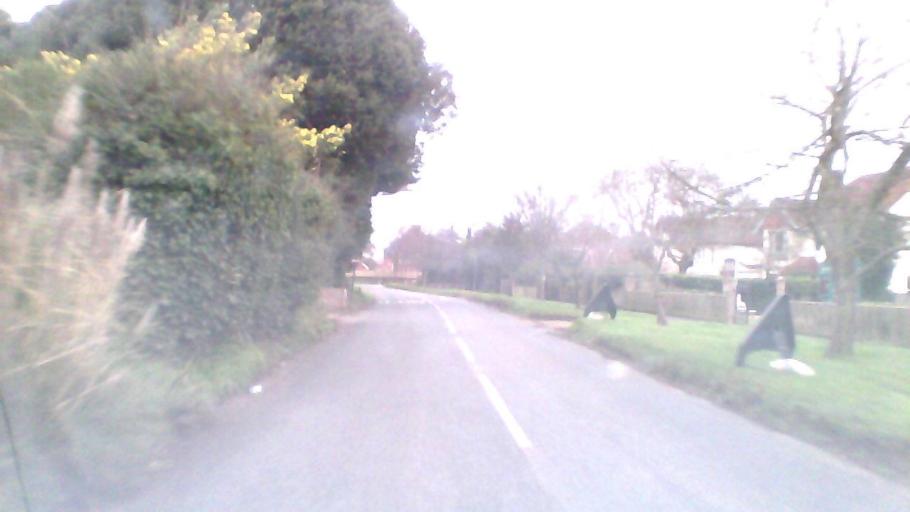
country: GB
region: England
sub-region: Isle of Wight
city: Bembridge
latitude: 50.6869
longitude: -1.0840
